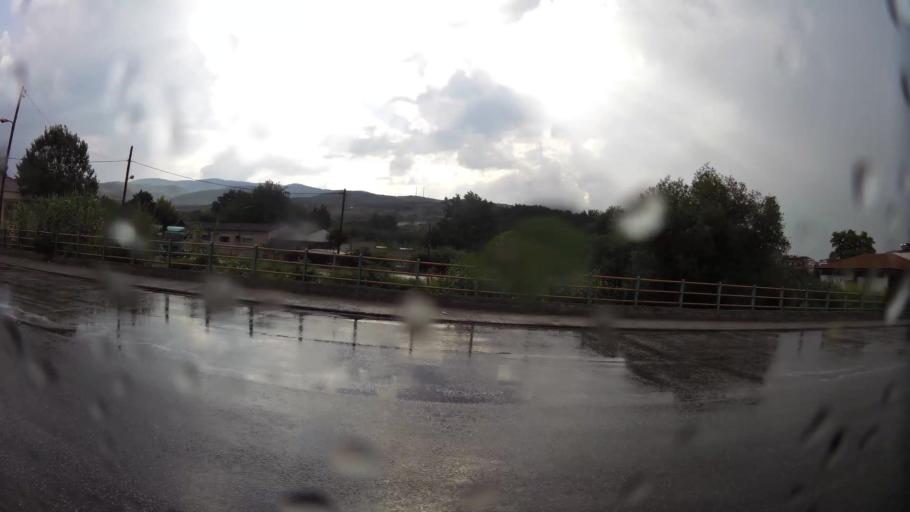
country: GR
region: Central Macedonia
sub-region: Nomos Imathias
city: Veroia
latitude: 40.5360
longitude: 22.2025
